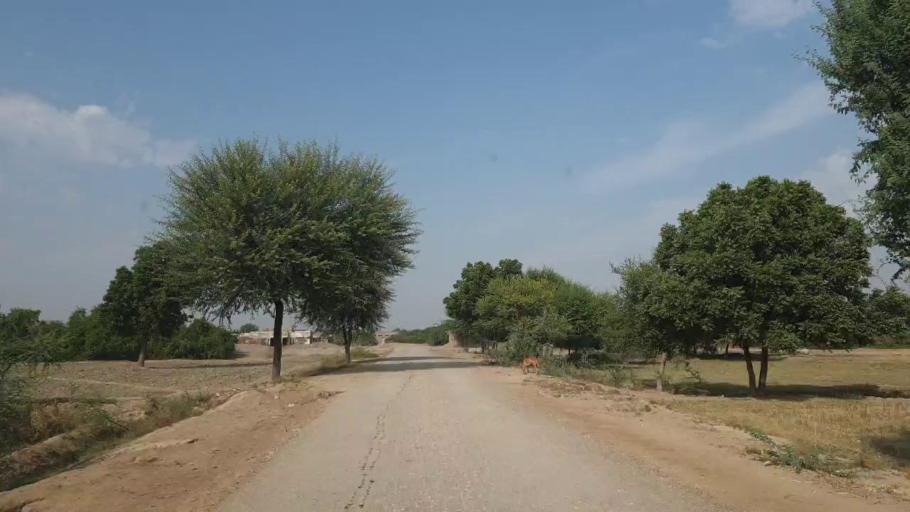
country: PK
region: Sindh
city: Digri
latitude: 25.0031
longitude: 69.0664
